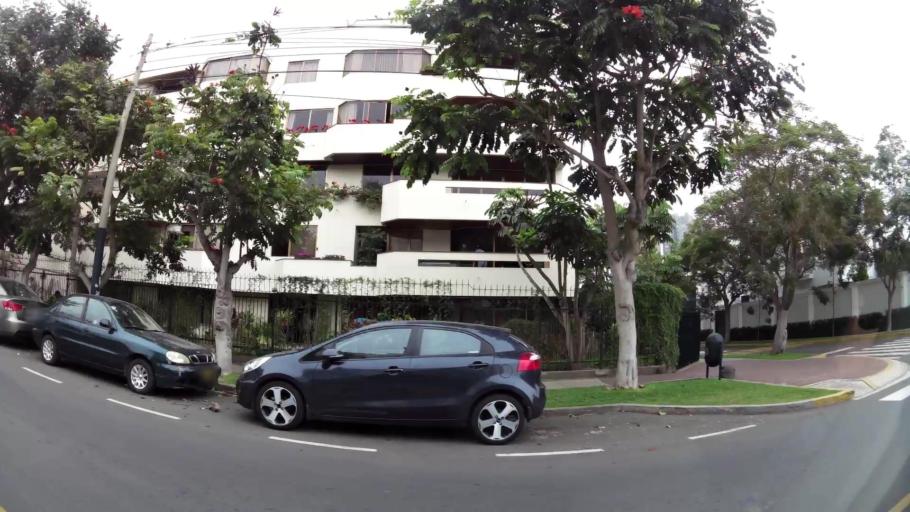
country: PE
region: Lima
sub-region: Lima
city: San Isidro
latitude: -12.0967
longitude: -77.0422
